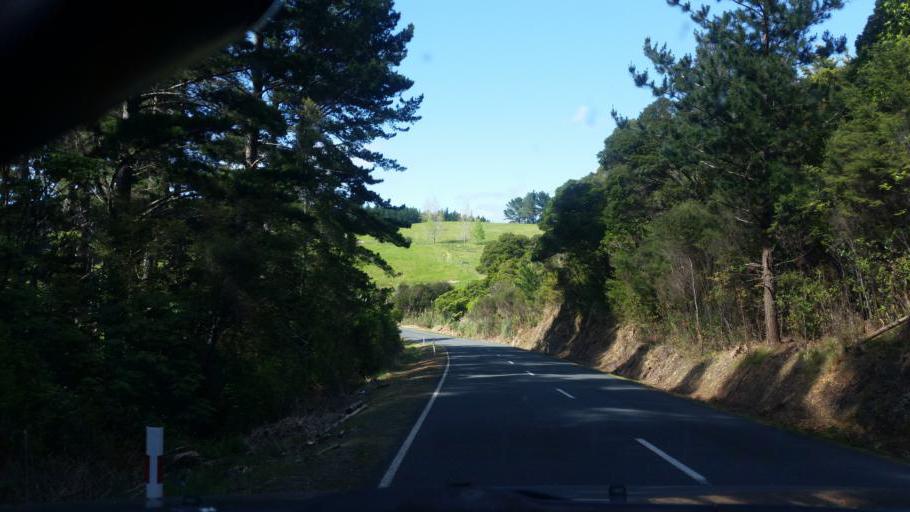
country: NZ
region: Northland
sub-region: Kaipara District
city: Dargaville
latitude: -35.7354
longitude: 173.8648
